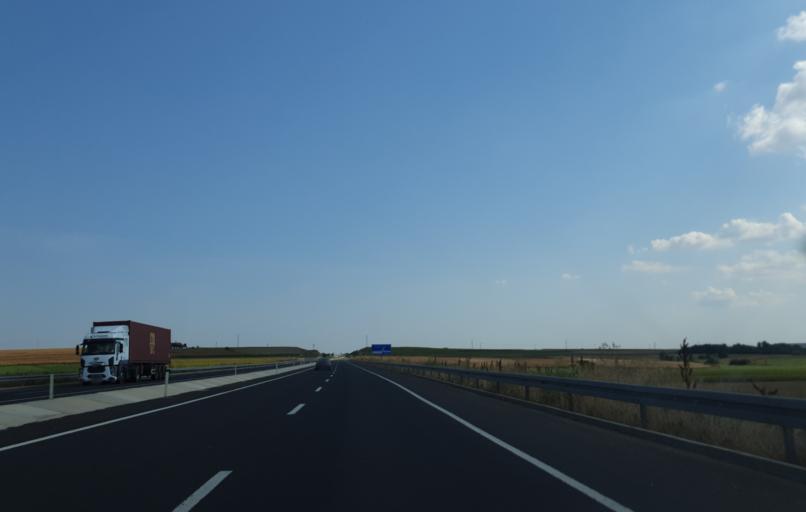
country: TR
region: Tekirdag
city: Muratli
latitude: 41.2167
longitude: 27.5329
